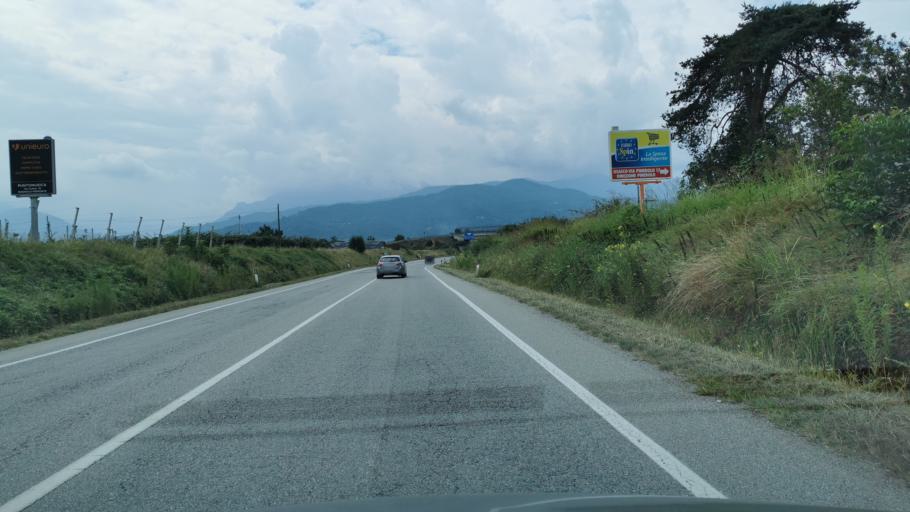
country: IT
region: Piedmont
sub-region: Provincia di Torino
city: Osasco
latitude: 44.8446
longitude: 7.3412
